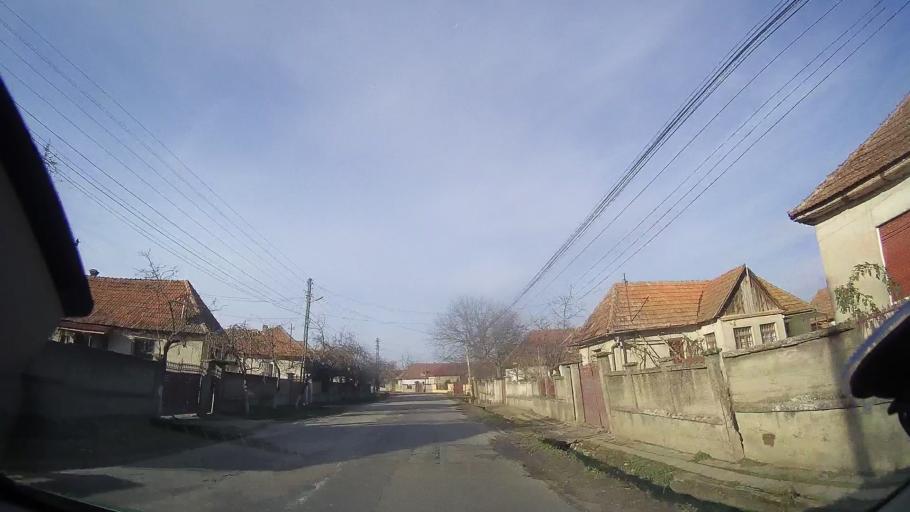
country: RO
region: Bihor
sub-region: Comuna Brusturi
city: Brusturi
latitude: 47.1464
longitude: 22.2566
